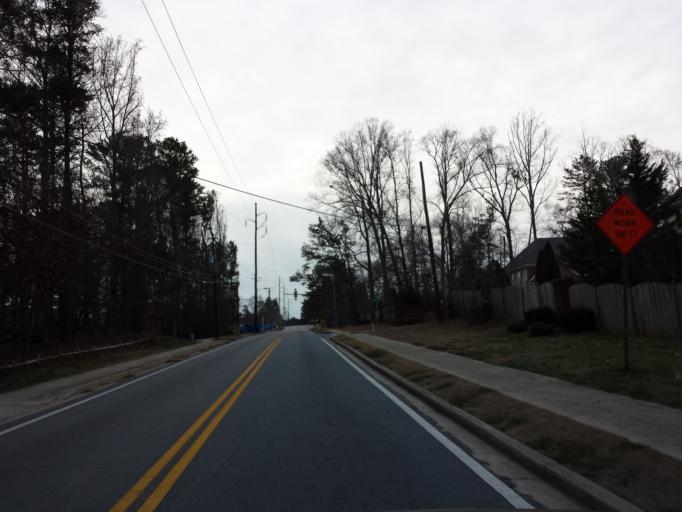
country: US
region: Georgia
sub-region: Cobb County
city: Marietta
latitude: 33.9568
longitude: -84.4778
